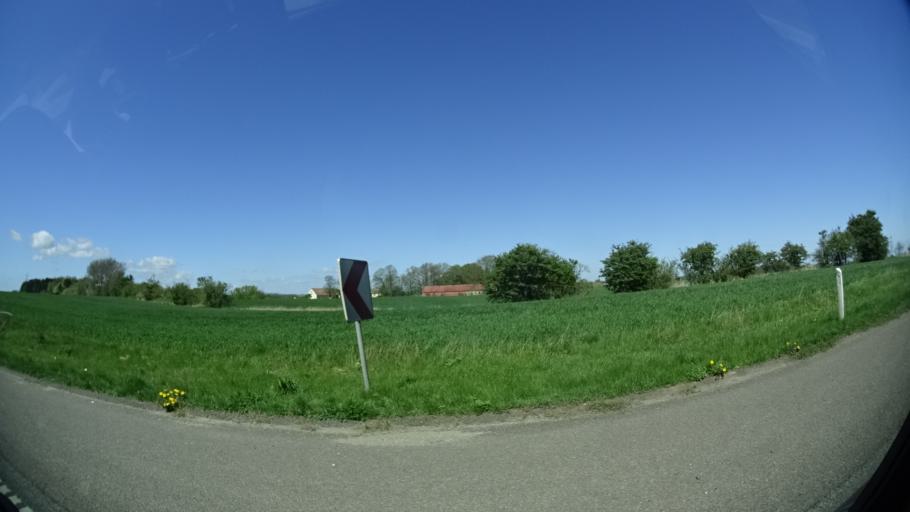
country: DK
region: Central Jutland
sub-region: Arhus Kommune
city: Kolt
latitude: 56.1216
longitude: 10.0816
